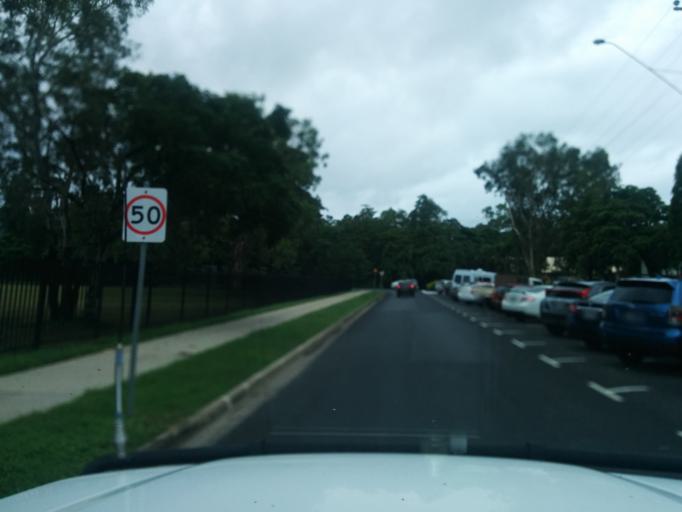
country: AU
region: Queensland
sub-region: Cairns
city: Cairns
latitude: -16.9208
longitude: 145.7538
